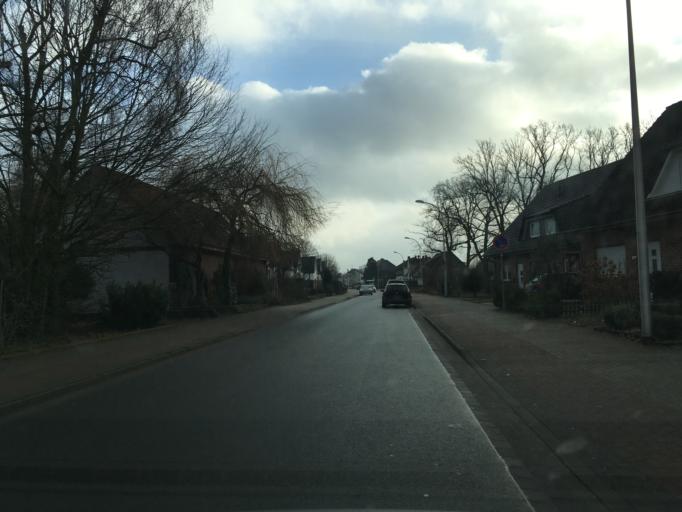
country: DE
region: North Rhine-Westphalia
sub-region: Regierungsbezirk Munster
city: Gronau
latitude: 52.2219
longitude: 7.0134
